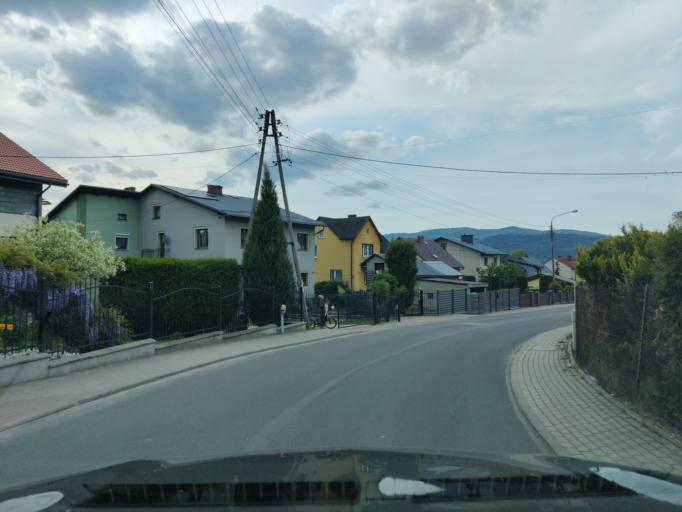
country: PL
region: Silesian Voivodeship
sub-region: Powiat zywiecki
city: Zywiec
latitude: 49.7088
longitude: 19.2091
